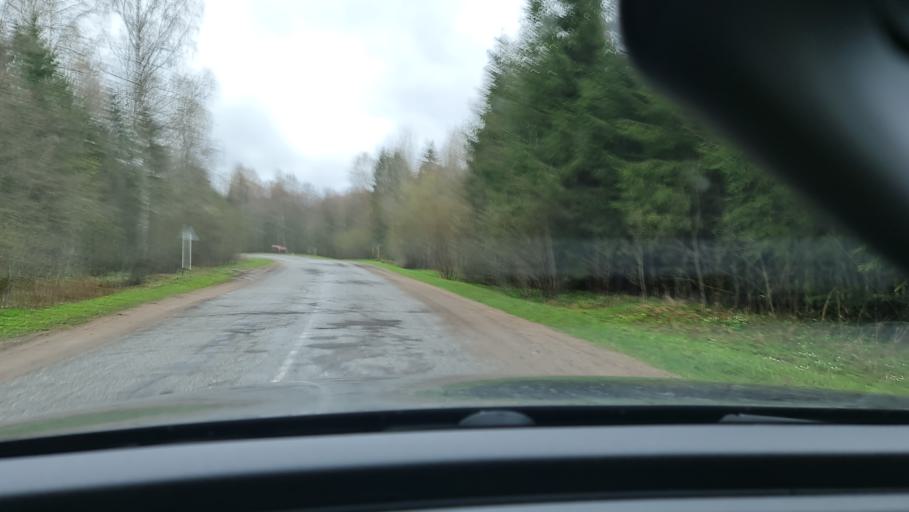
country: RU
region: Novgorod
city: Marevo
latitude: 57.2609
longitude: 32.0678
